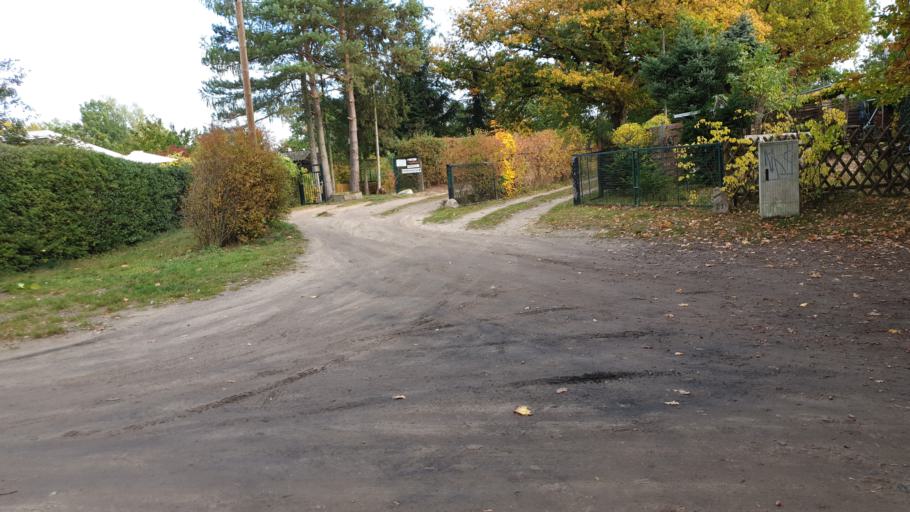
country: DE
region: Brandenburg
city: Joachimsthal
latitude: 52.9654
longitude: 13.7533
